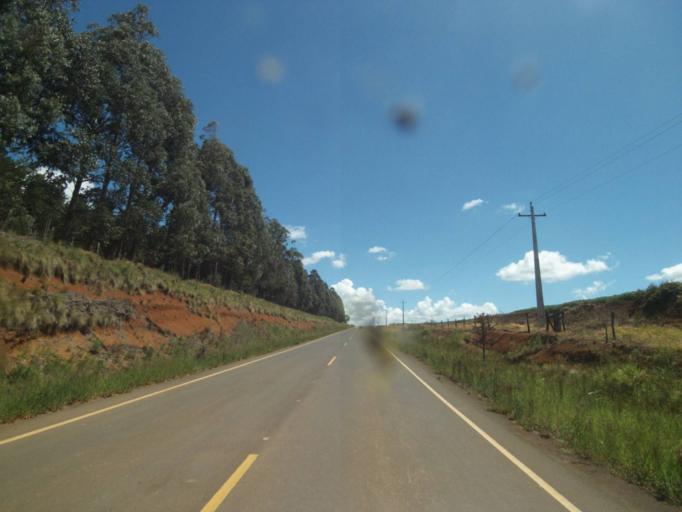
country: BR
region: Parana
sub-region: Pinhao
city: Pinhao
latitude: -25.8301
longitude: -52.0195
